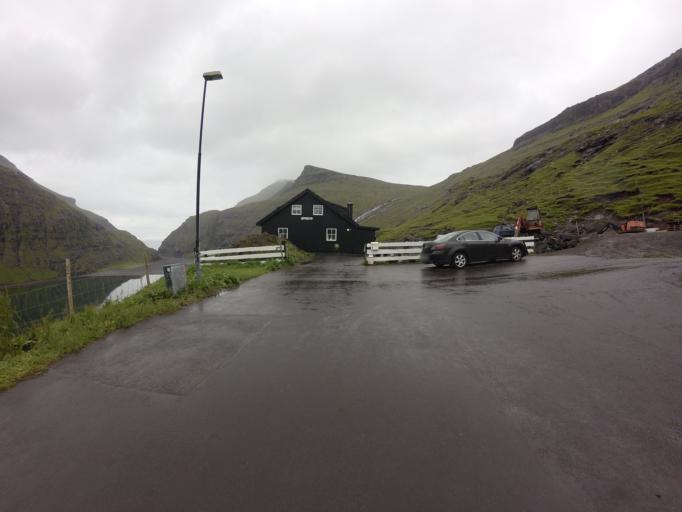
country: FO
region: Streymoy
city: Vestmanna
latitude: 62.2485
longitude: -7.1800
